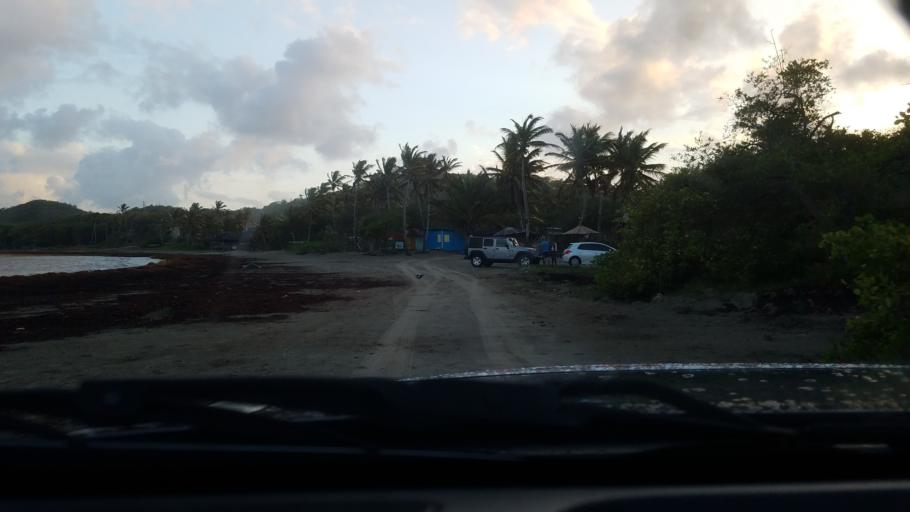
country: LC
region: Gros-Islet
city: Gros Islet
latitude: 14.0912
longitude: -60.9267
